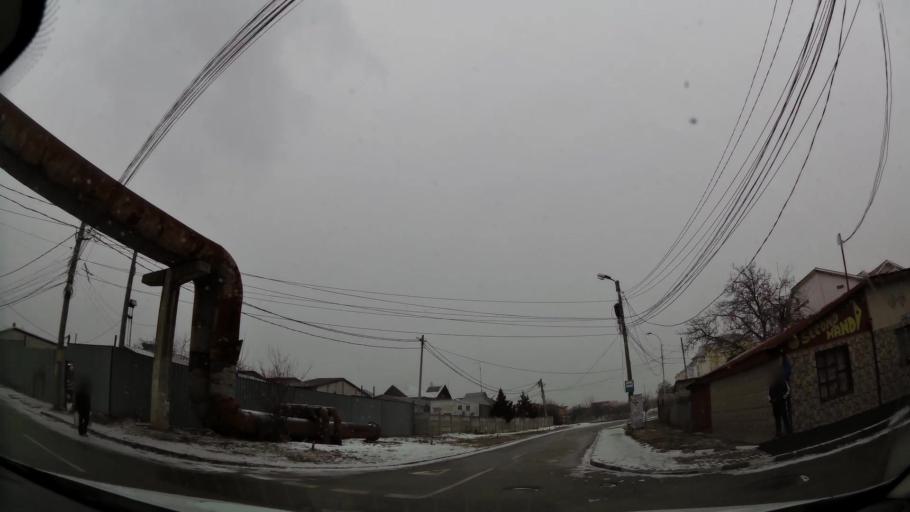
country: RO
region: Dambovita
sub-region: Municipiul Targoviste
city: Targoviste
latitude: 44.9338
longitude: 25.4434
